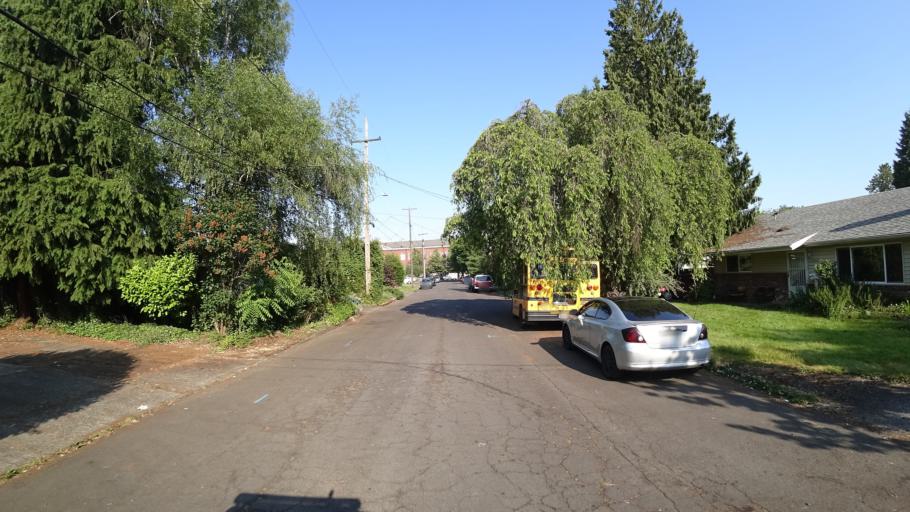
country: US
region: Oregon
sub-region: Washington County
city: West Haven
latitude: 45.5891
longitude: -122.7355
